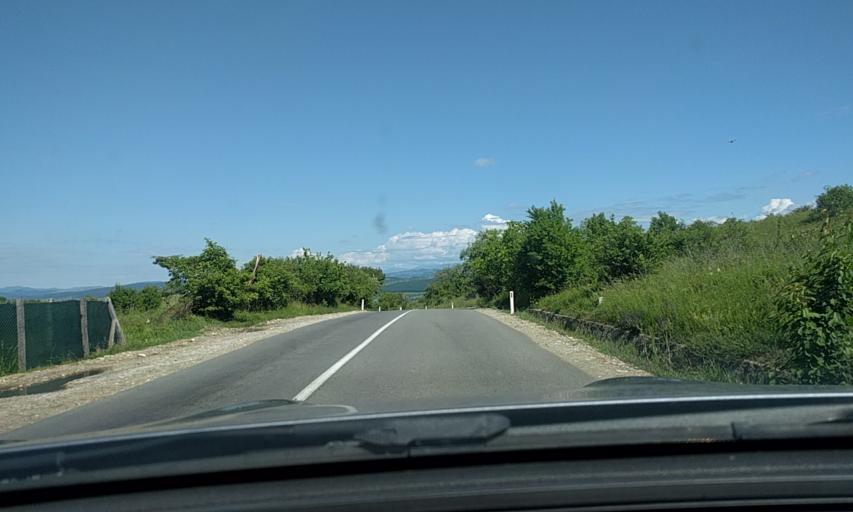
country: RO
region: Bistrita-Nasaud
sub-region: Comuna Dumitra
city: Dumitra
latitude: 47.1982
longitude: 24.4830
